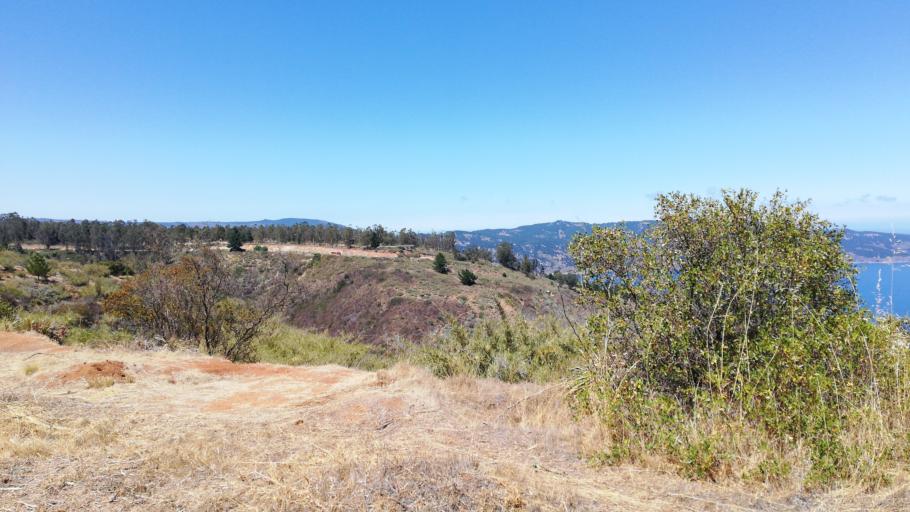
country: CL
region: Valparaiso
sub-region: Provincia de Valparaiso
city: Valparaiso
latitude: -33.0747
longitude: -71.6576
